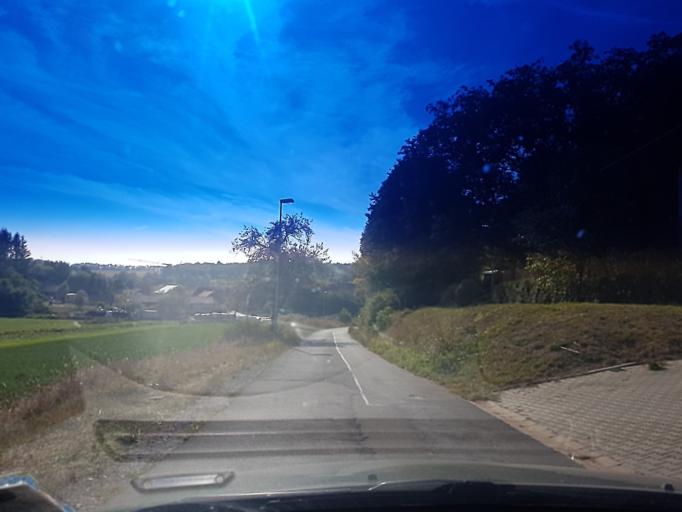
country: DE
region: Bavaria
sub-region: Upper Franconia
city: Schlusselfeld
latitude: 49.7828
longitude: 10.6070
